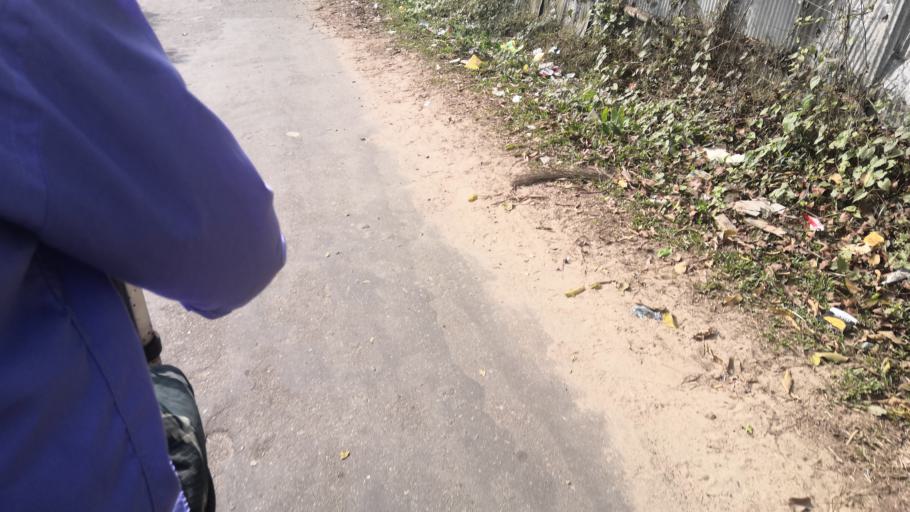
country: BD
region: Chittagong
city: Chittagong
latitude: 22.4732
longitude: 91.7860
